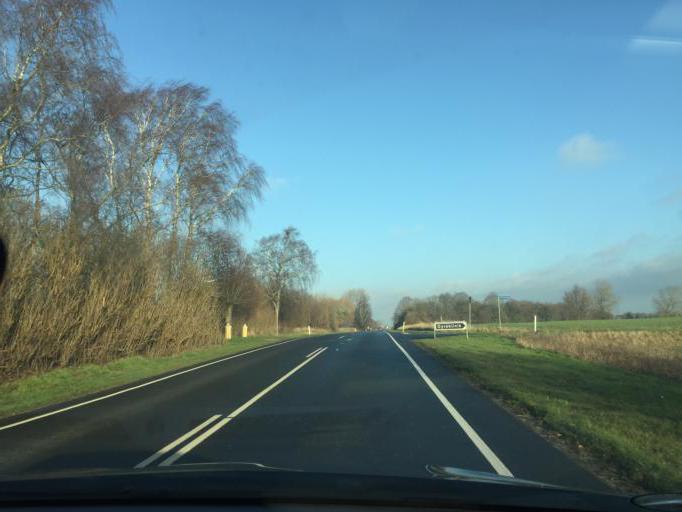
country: DK
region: South Denmark
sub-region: Faaborg-Midtfyn Kommune
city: Faaborg
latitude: 55.1783
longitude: 10.2950
